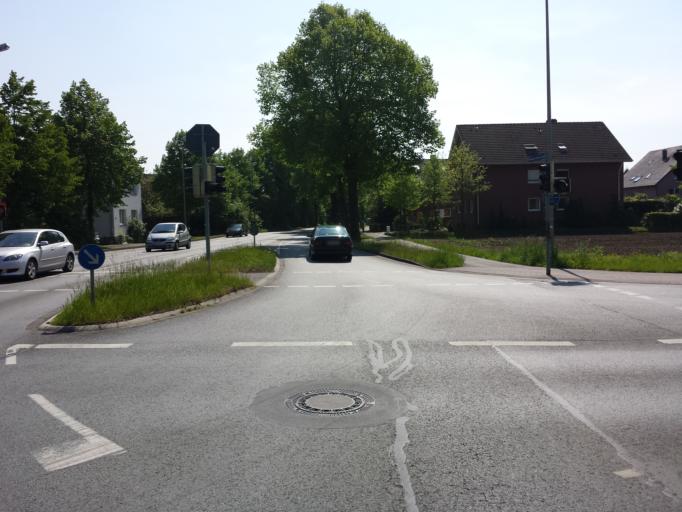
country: DE
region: North Rhine-Westphalia
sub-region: Regierungsbezirk Detmold
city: Guetersloh
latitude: 51.8865
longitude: 8.3890
